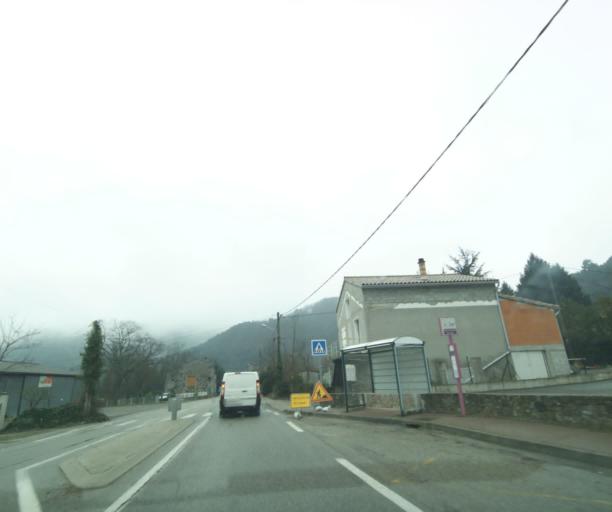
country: FR
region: Rhone-Alpes
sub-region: Departement de l'Ardeche
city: Jaujac
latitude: 44.6618
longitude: 4.2965
